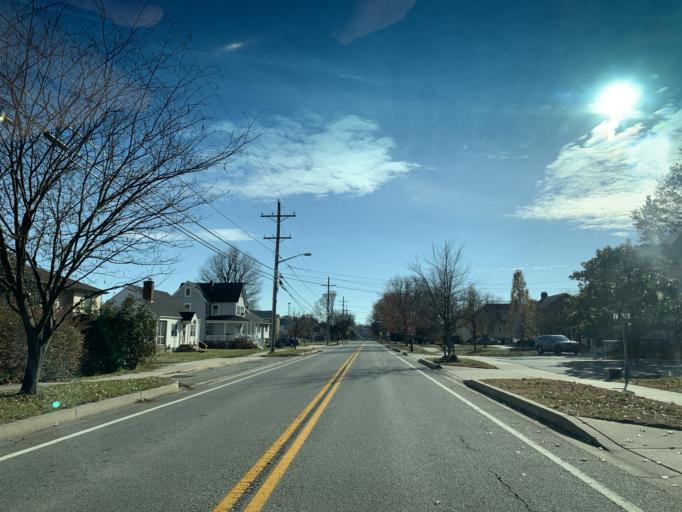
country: US
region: Maryland
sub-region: Cecil County
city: Perryville
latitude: 39.5659
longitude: -76.0708
